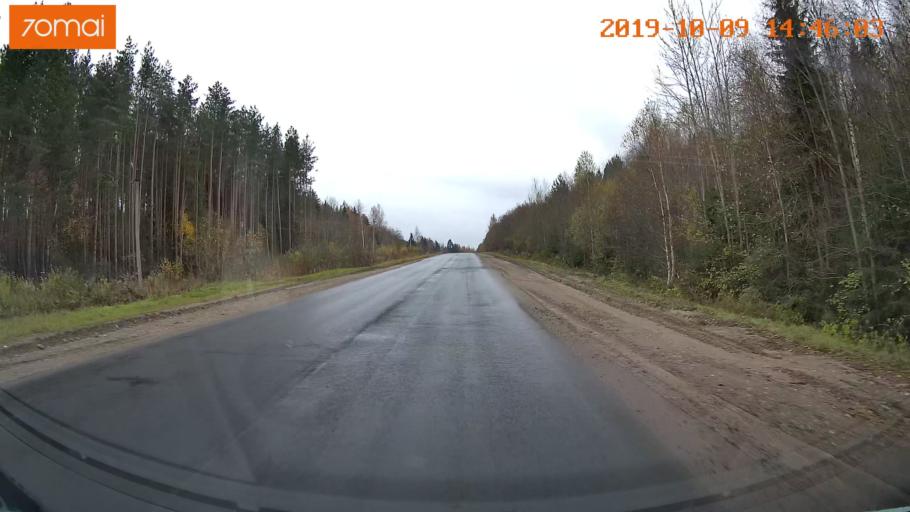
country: RU
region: Kostroma
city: Buy
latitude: 58.4362
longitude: 41.5772
